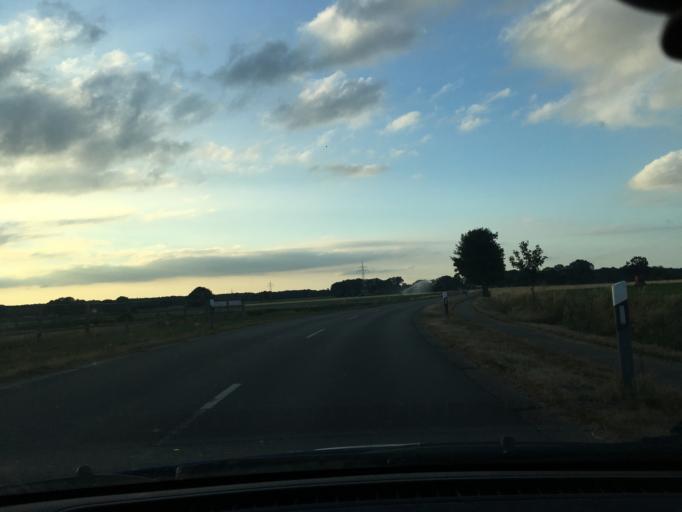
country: DE
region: Lower Saxony
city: Soderstorf
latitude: 53.1655
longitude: 10.1583
